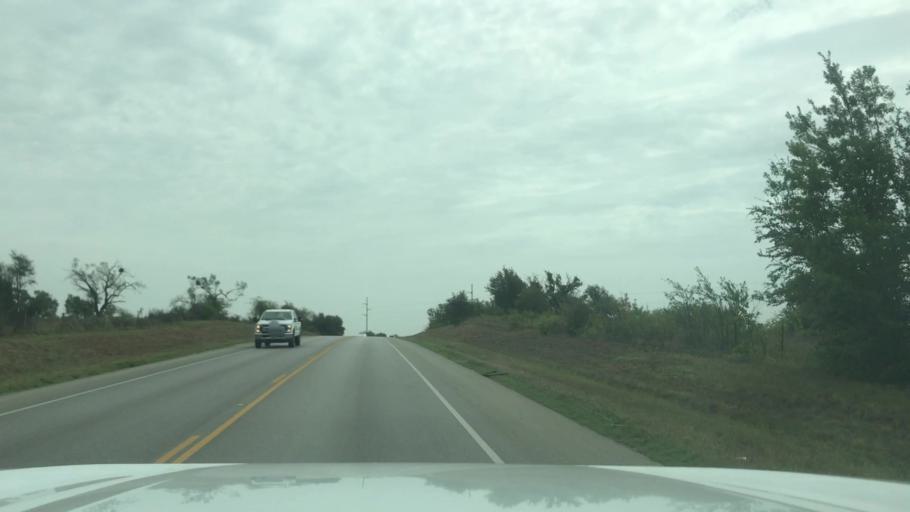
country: US
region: Texas
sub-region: Erath County
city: Dublin
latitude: 32.0977
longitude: -98.3850
